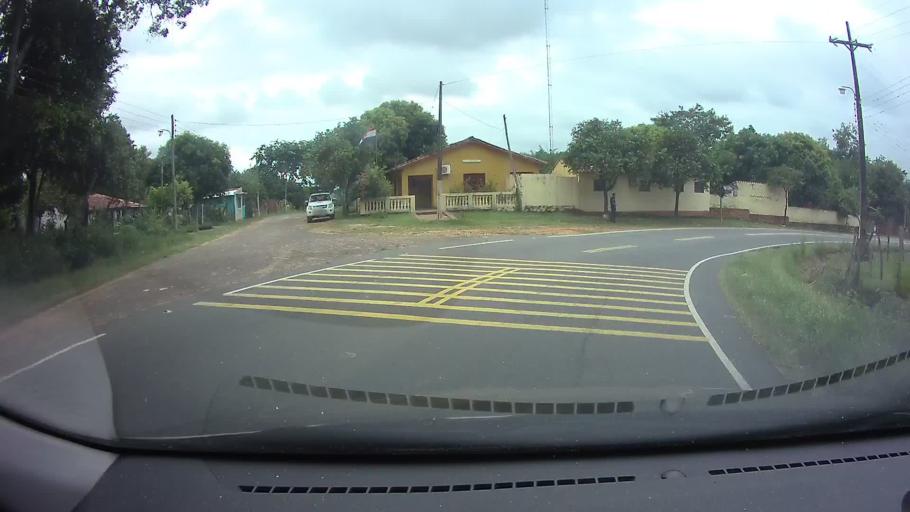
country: PY
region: Central
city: Nueva Italia
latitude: -25.6037
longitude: -57.4148
